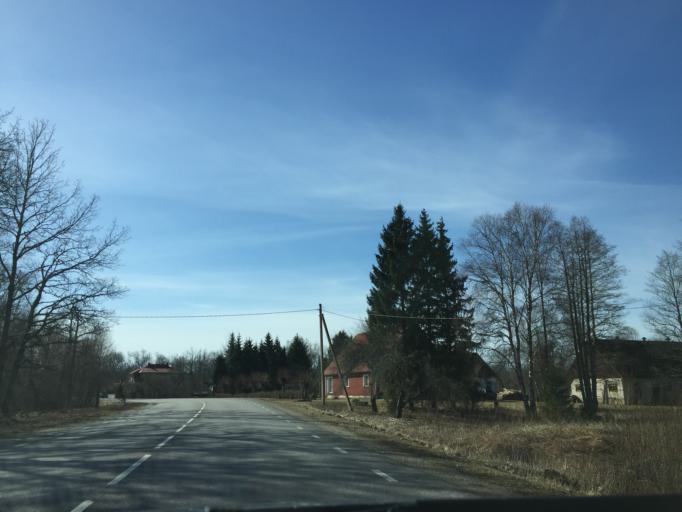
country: EE
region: Laeaene
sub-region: Lihula vald
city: Lihula
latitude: 58.6188
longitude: 23.6919
